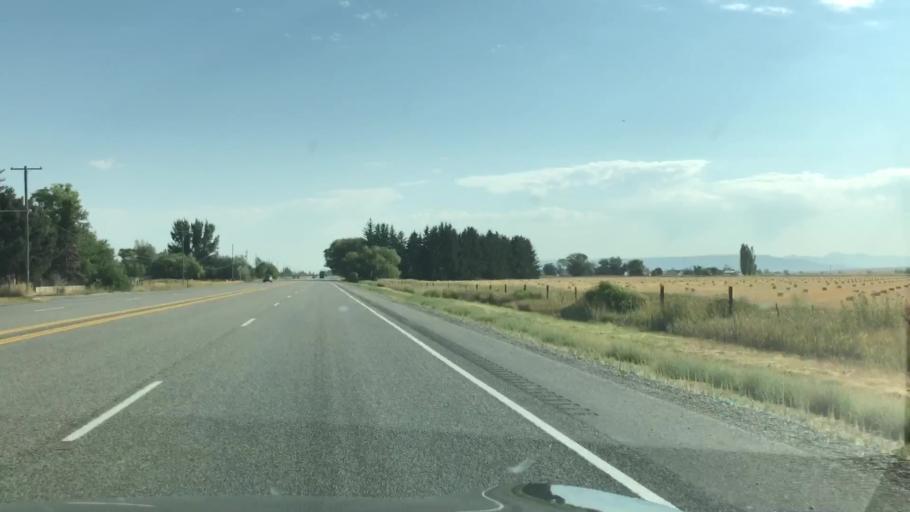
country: US
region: Idaho
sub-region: Bonneville County
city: Iona
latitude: 43.5841
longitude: -111.8926
